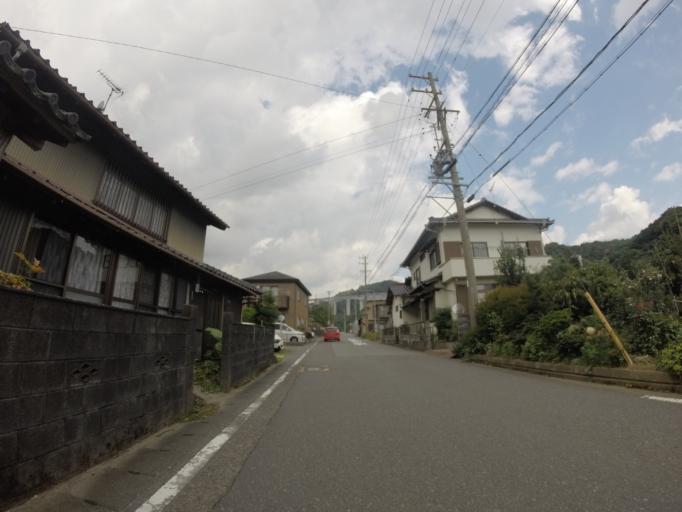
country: JP
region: Shizuoka
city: Shizuoka-shi
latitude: 35.0656
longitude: 138.4696
